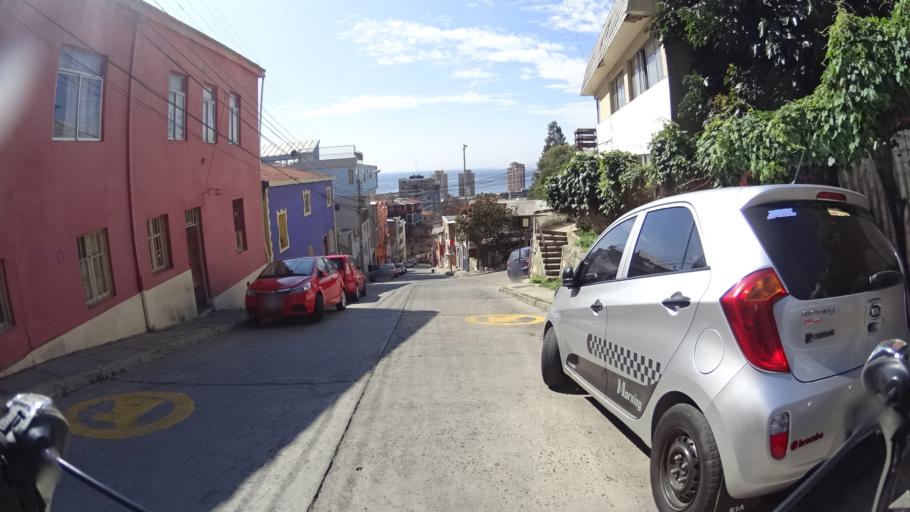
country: CL
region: Valparaiso
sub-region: Provincia de Valparaiso
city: Valparaiso
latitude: -33.0496
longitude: -71.6209
